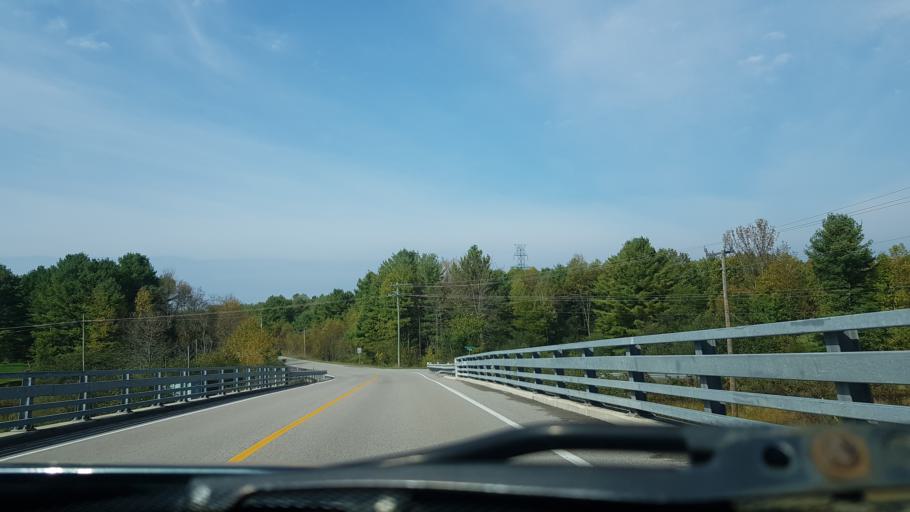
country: CA
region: Ontario
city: Gravenhurst
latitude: 44.7752
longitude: -79.2966
